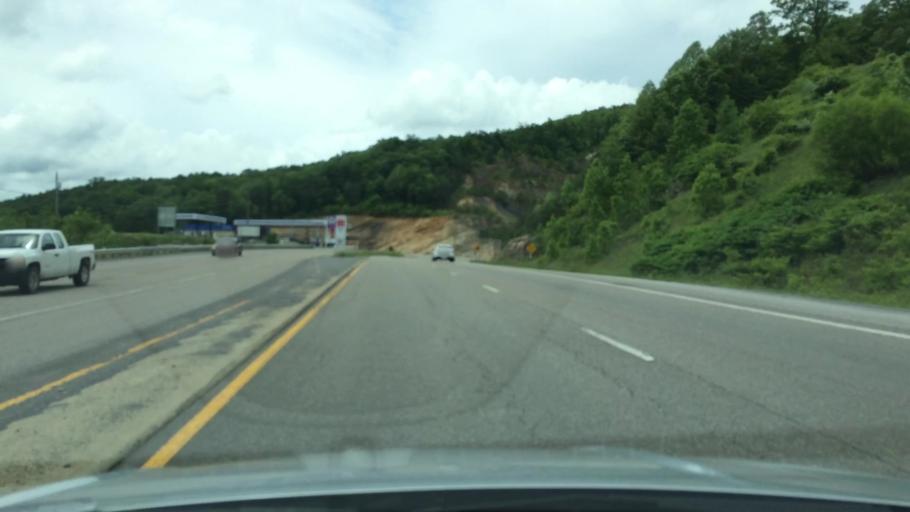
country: US
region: Kentucky
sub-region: Letcher County
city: Jenkins
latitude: 37.1556
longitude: -82.6293
